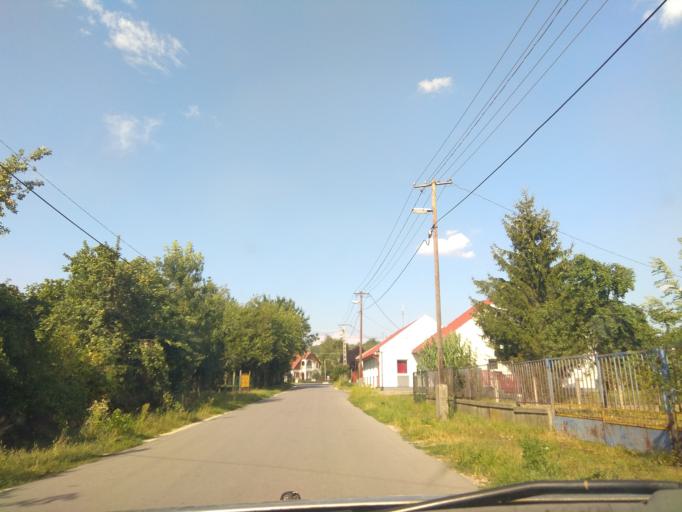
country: HU
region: Borsod-Abauj-Zemplen
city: Emod
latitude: 47.9420
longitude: 20.8131
